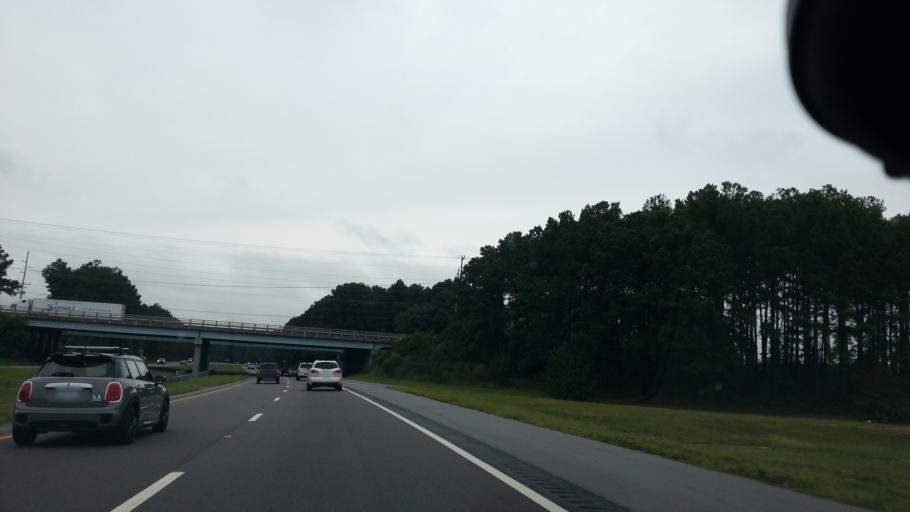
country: US
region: North Carolina
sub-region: Cumberland County
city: Fort Bragg
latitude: 35.0760
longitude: -78.9587
